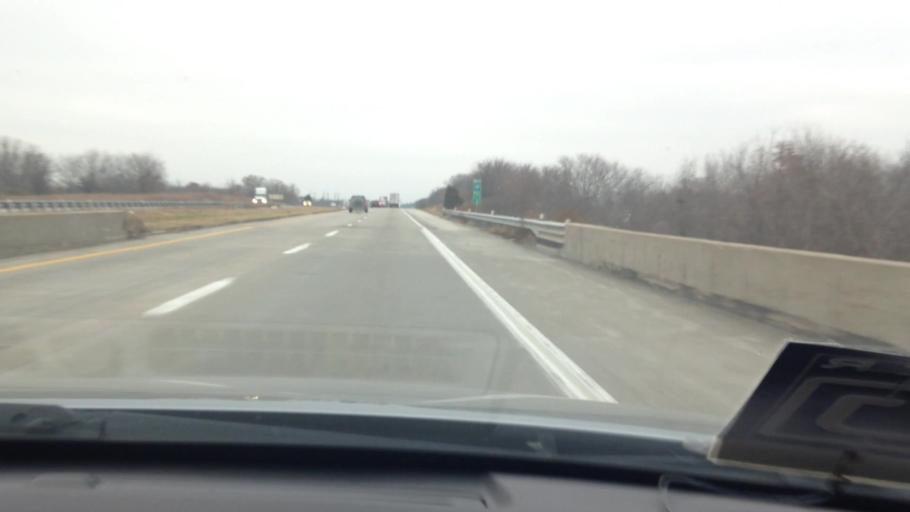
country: US
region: Missouri
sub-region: Cass County
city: Raymore
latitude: 38.7708
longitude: -94.4916
